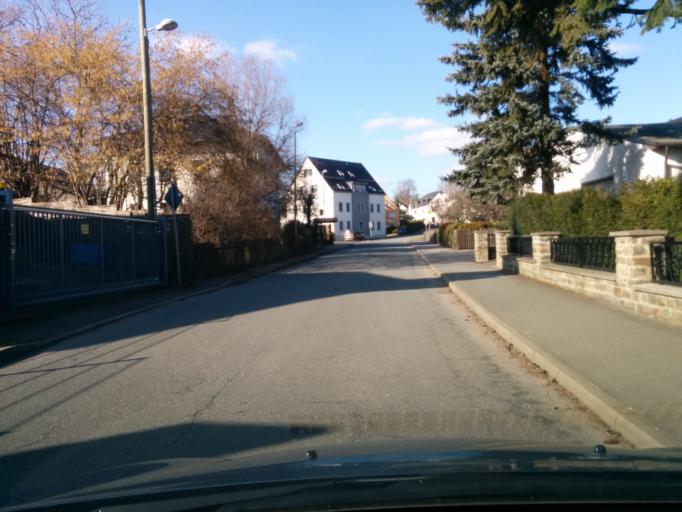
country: DE
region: Saxony
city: Neukirchen
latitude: 50.7861
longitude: 12.8490
